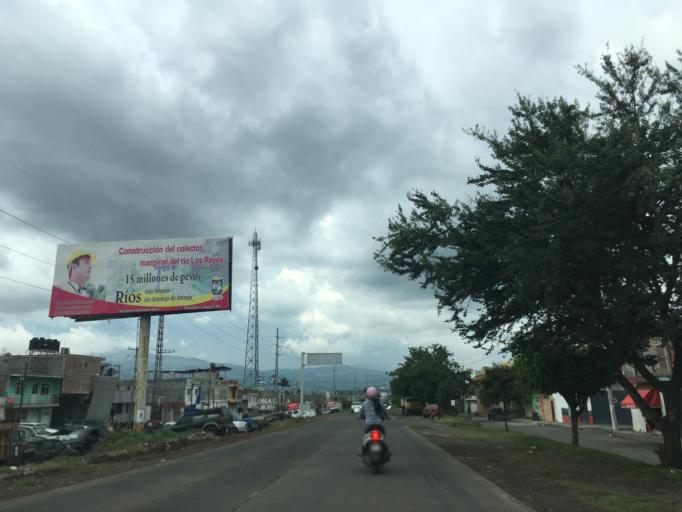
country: MX
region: Michoacan
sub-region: Los Reyes
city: La Higuerita (Colonia San Rafael)
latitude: 19.5919
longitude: -102.4789
